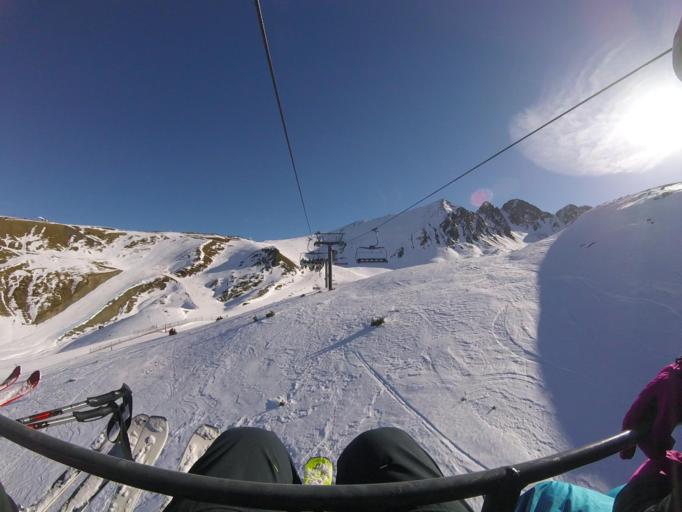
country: AD
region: Encamp
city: Pas de la Casa
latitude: 42.5280
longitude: 1.7109
